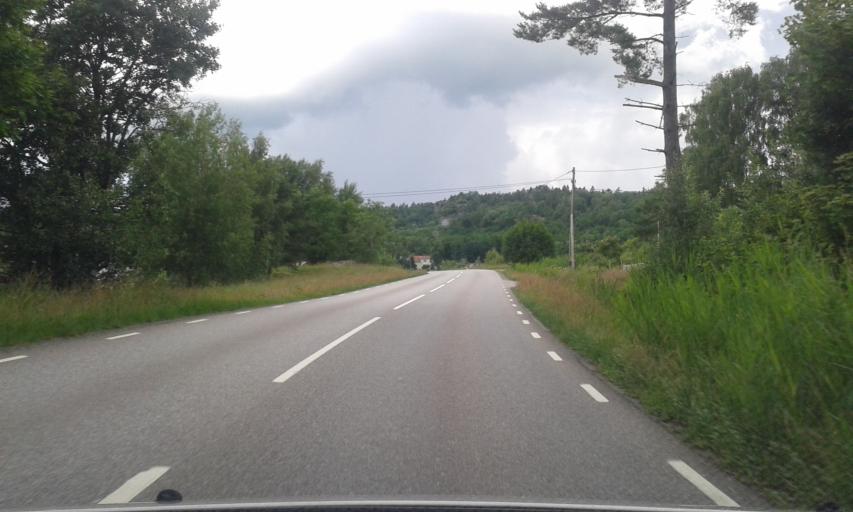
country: SE
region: Vaestra Goetaland
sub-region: Kungalvs Kommun
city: Kode
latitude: 57.9245
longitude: 11.9098
